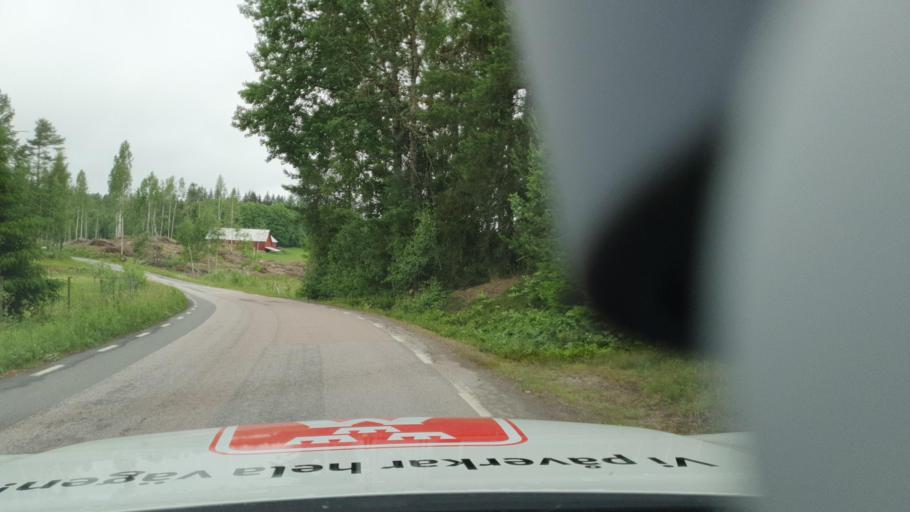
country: SE
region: Vaestra Goetaland
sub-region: Gullspangs Kommun
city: Gullspang
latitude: 59.0333
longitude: 14.1620
